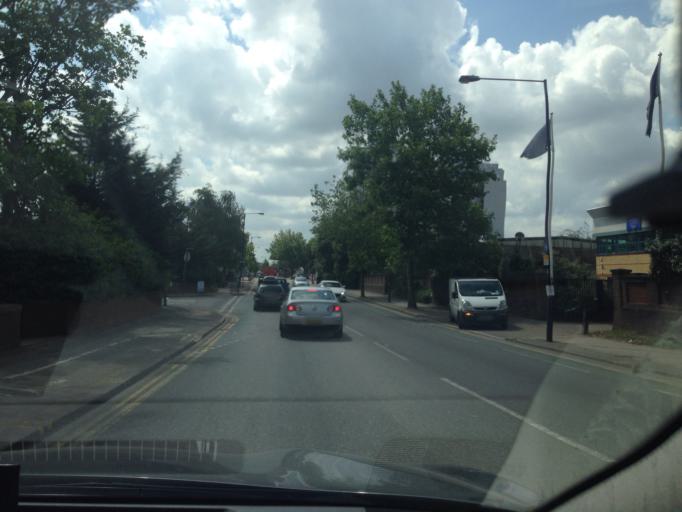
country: GB
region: England
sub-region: Greater London
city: Acton
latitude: 51.5350
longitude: -0.2750
